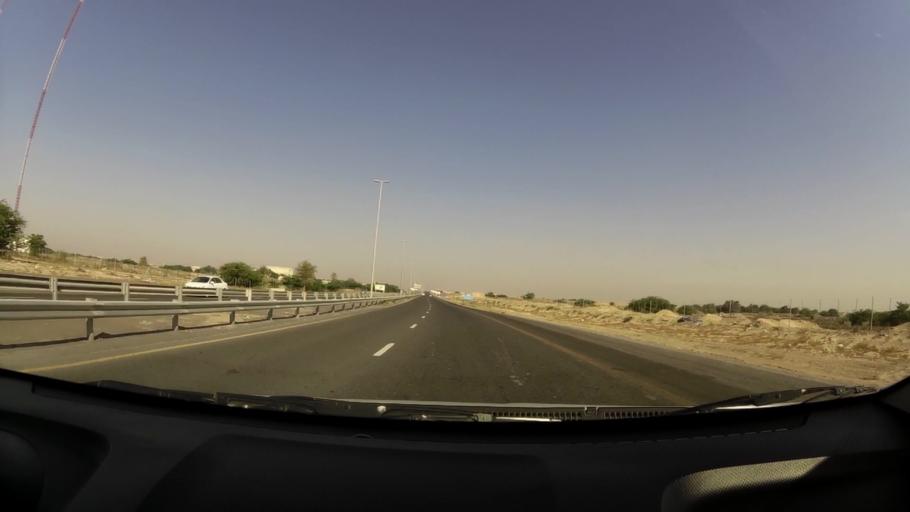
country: AE
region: Umm al Qaywayn
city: Umm al Qaywayn
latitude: 25.4856
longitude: 55.5550
